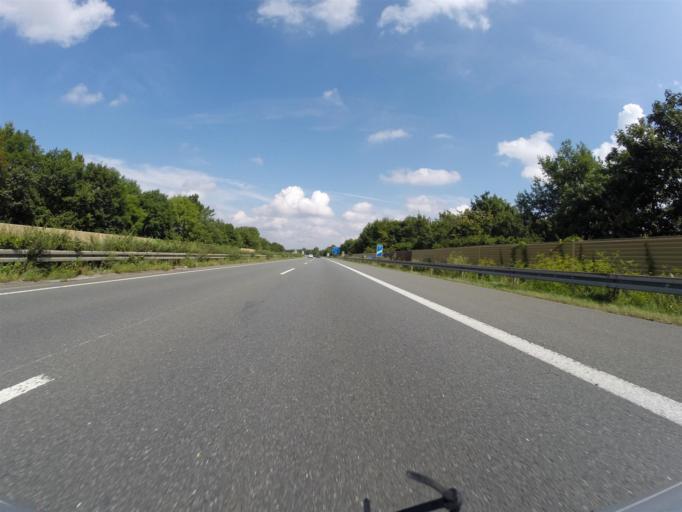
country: DE
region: North Rhine-Westphalia
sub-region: Regierungsbezirk Detmold
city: Hovelhof
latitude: 51.7835
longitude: 8.7040
